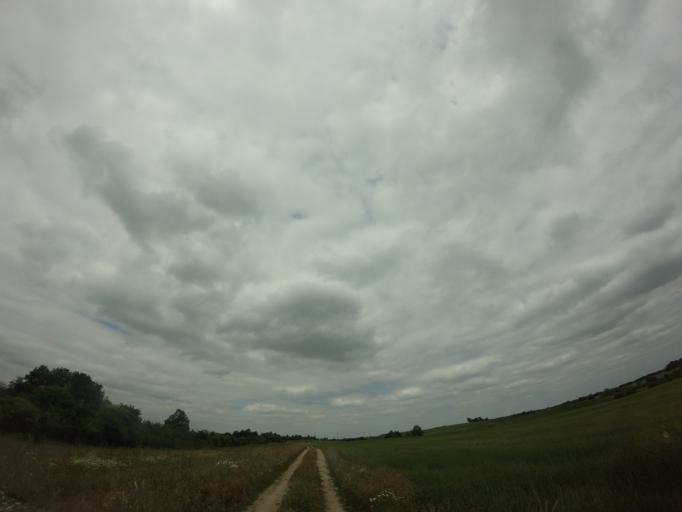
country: PL
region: West Pomeranian Voivodeship
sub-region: Powiat choszczenski
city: Krzecin
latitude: 53.0575
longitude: 15.5217
